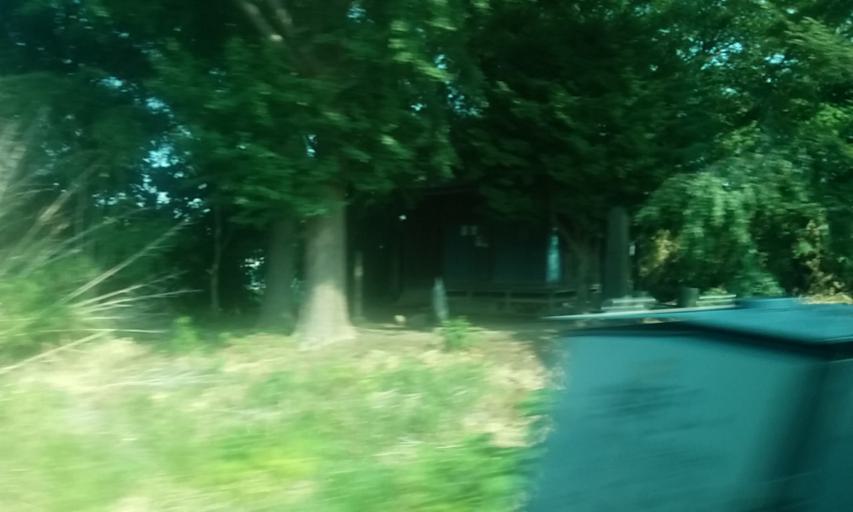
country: JP
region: Saitama
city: Shiraoka
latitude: 36.0265
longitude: 139.6677
